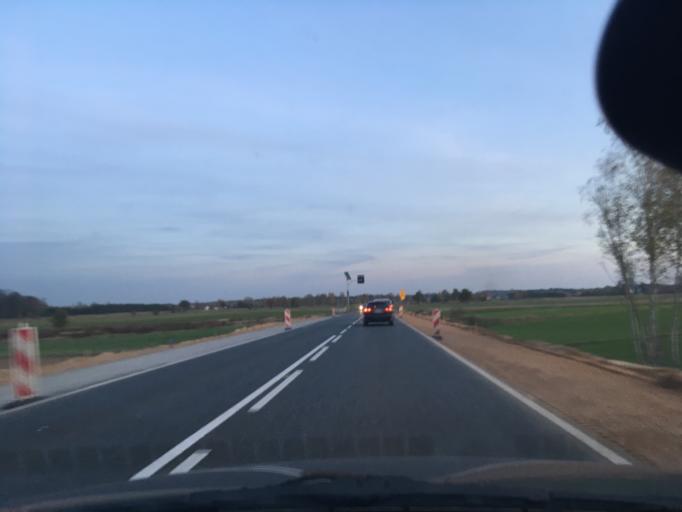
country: PL
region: Masovian Voivodeship
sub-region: Powiat plocki
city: Wyszogrod
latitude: 52.3615
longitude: 20.1993
